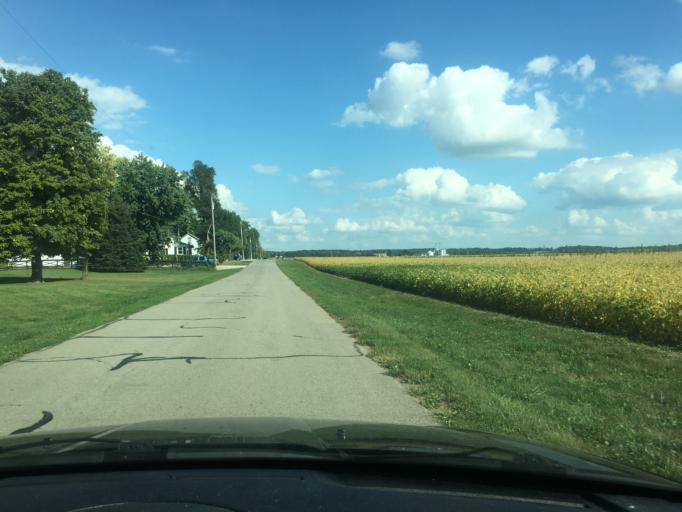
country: US
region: Ohio
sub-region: Logan County
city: West Liberty
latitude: 40.2484
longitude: -83.7538
